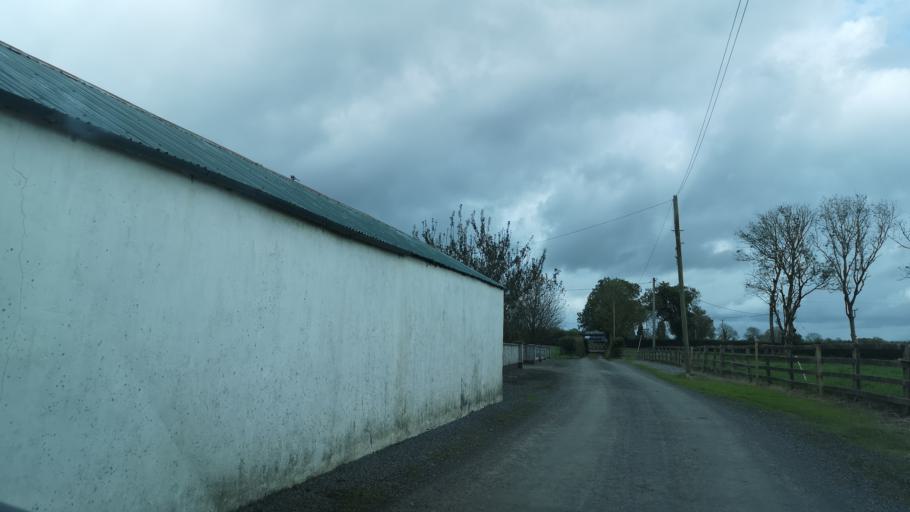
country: IE
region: Connaught
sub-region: County Galway
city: Athenry
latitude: 53.2997
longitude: -8.6817
